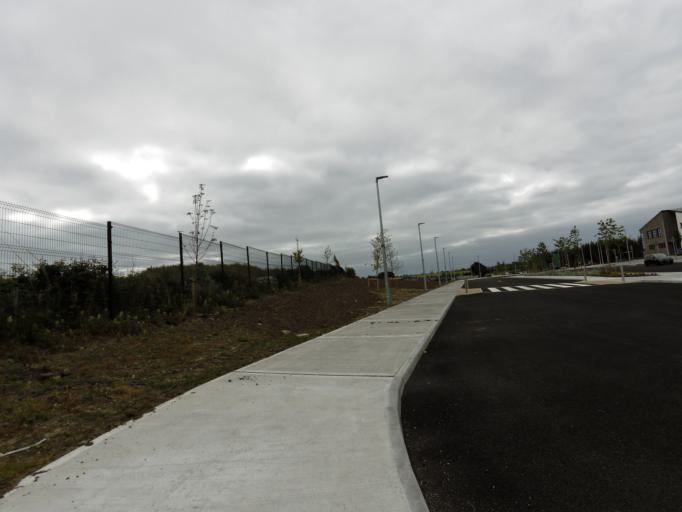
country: IE
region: Connaught
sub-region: County Galway
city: Athenry
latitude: 53.2933
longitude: -8.7534
